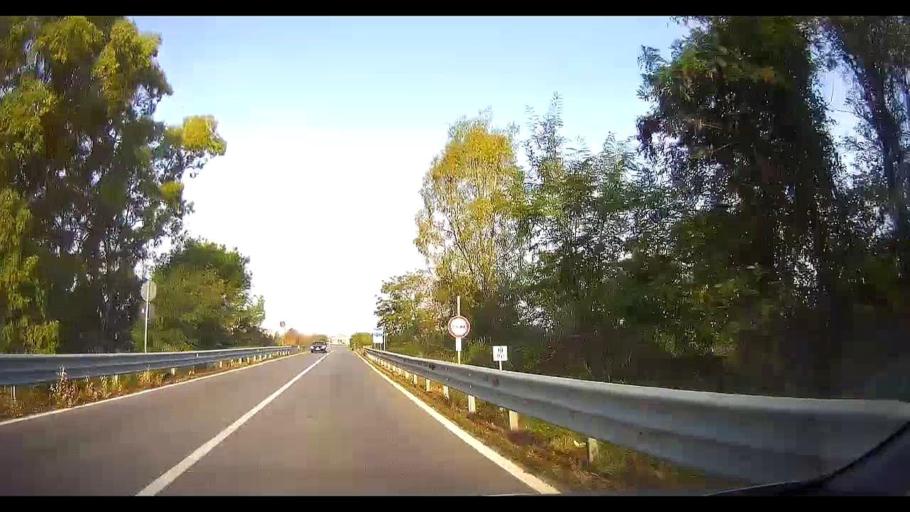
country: IT
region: Calabria
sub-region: Provincia di Cosenza
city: Cariati
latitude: 39.5217
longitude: 16.9006
